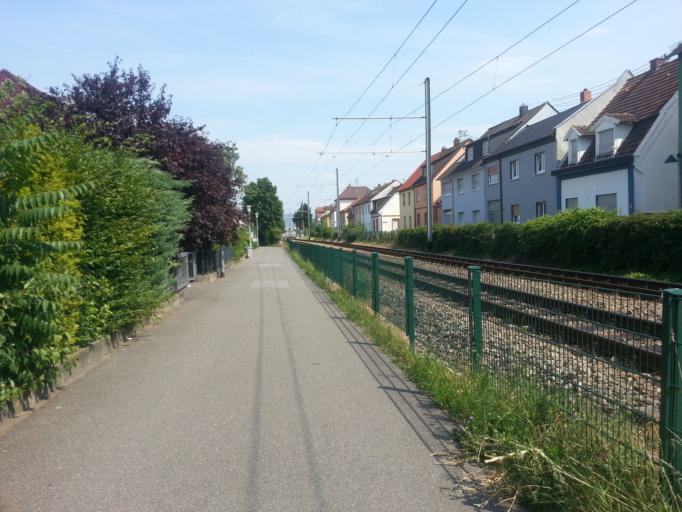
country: DE
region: Baden-Wuerttemberg
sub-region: Karlsruhe Region
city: Ilvesheim
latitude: 49.4980
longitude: 8.5514
